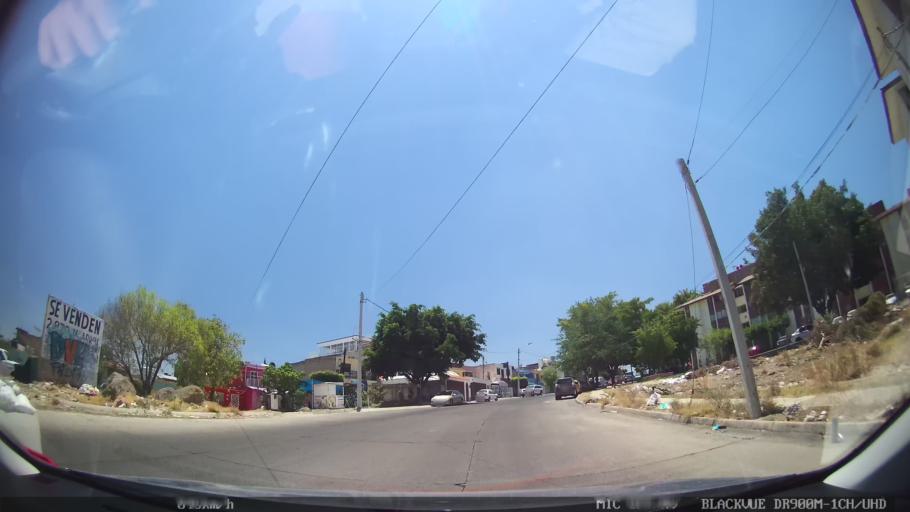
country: MX
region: Jalisco
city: Tlaquepaque
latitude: 20.6866
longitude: -103.2814
